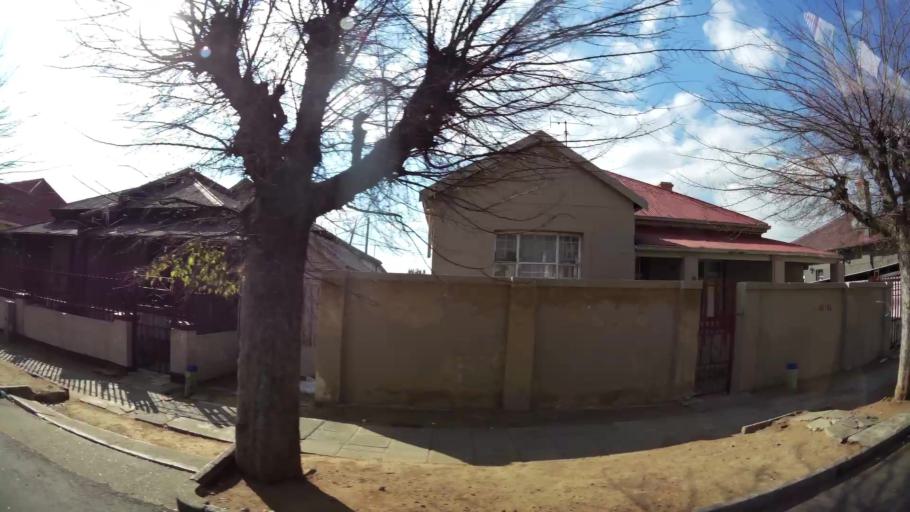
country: ZA
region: Gauteng
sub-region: West Rand District Municipality
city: Krugersdorp
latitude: -26.1073
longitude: 27.7748
